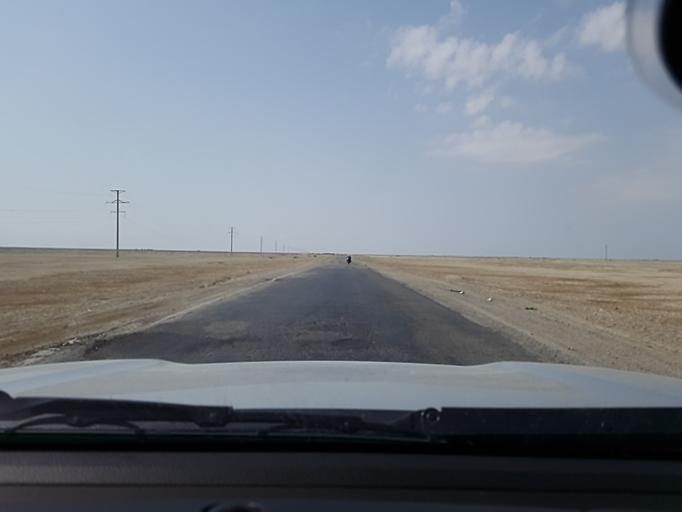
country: TM
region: Balkan
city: Gumdag
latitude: 39.0502
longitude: 54.5843
